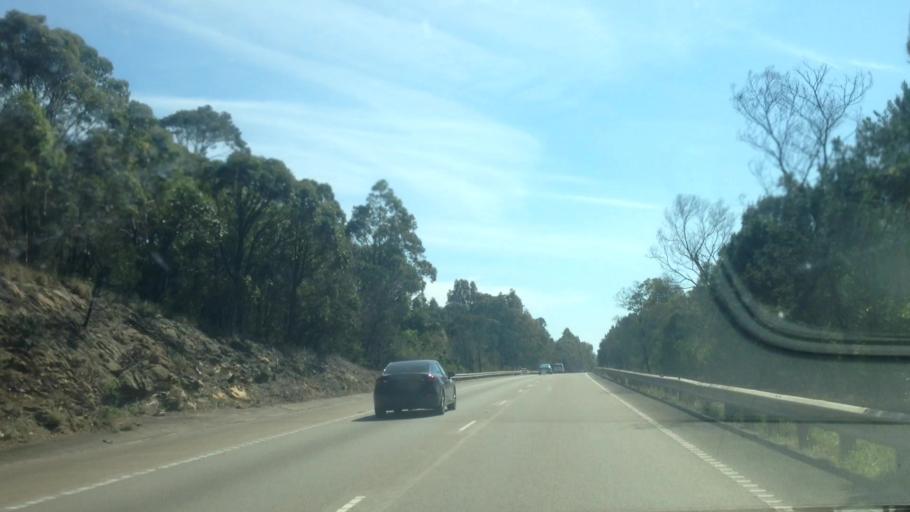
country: AU
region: New South Wales
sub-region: Lake Macquarie Shire
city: Fennell Bay
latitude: -32.9614
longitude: 151.5396
